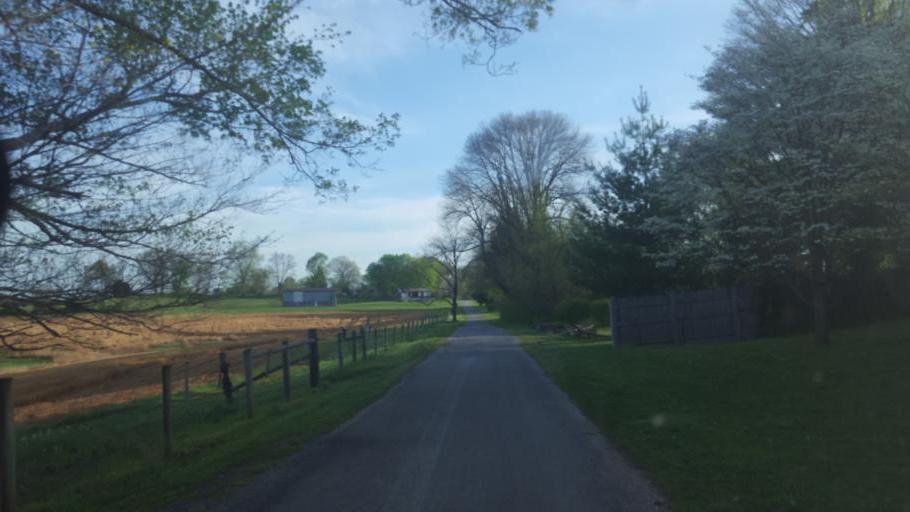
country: US
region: Kentucky
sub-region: Hart County
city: Munfordville
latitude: 37.2568
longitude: -85.8880
